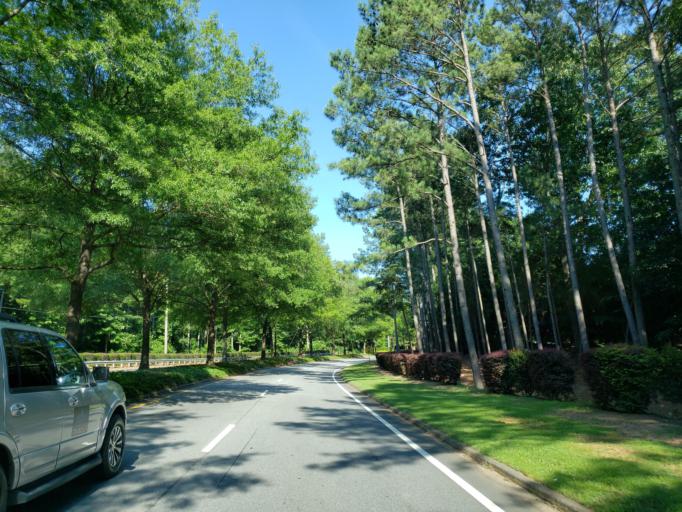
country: US
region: Georgia
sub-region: Cherokee County
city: Woodstock
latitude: 34.1314
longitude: -84.5626
